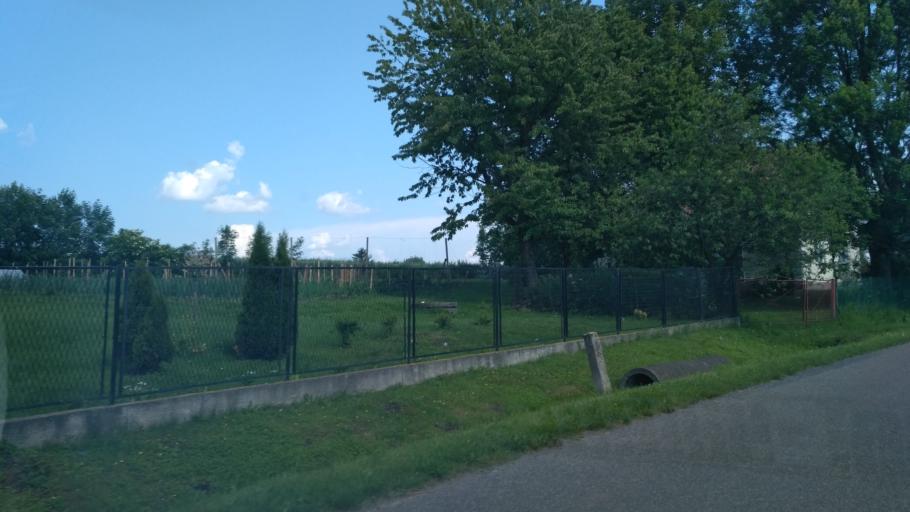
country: PL
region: Subcarpathian Voivodeship
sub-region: Powiat jaroslawski
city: Rokietnica
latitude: 49.9410
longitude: 22.7076
